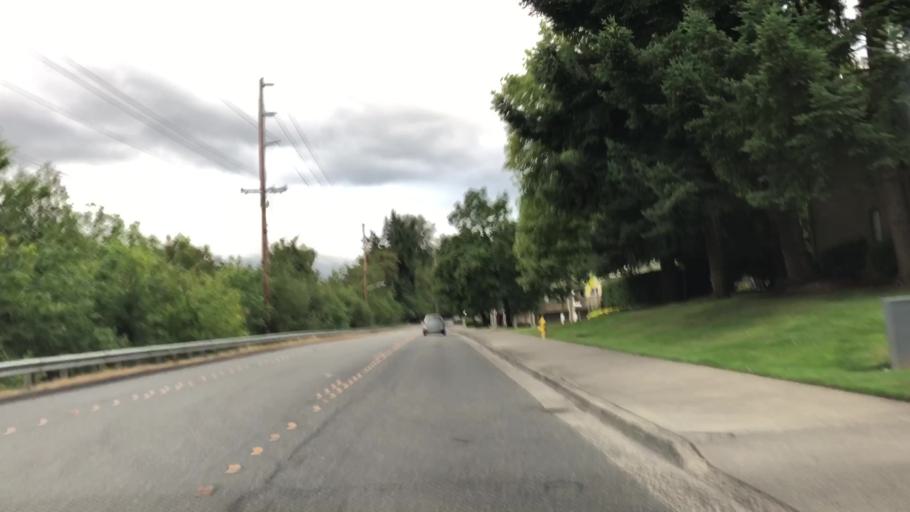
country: US
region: Washington
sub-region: King County
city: Redmond
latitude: 47.6793
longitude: -122.1395
